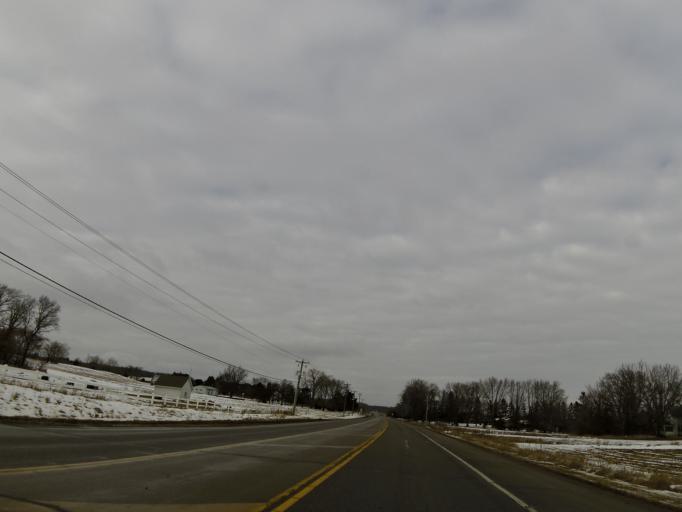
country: US
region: Minnesota
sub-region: Washington County
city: Bayport
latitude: 44.9992
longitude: -92.7918
